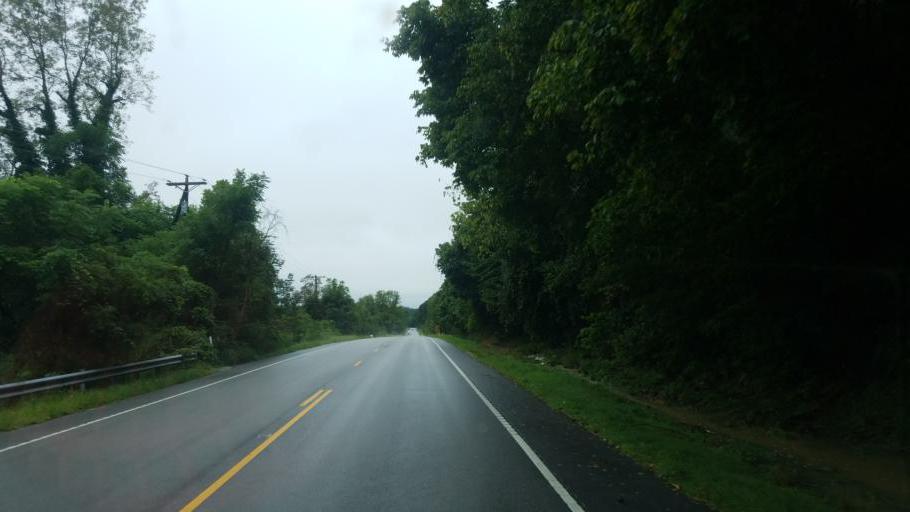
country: US
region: Ohio
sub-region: Adams County
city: Manchester
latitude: 38.6673
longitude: -83.6382
